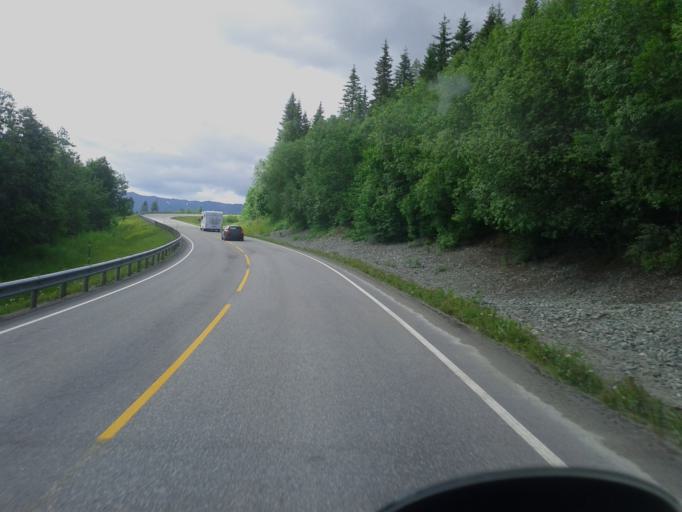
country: NO
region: Nord-Trondelag
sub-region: Grong
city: Grong
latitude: 64.5393
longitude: 12.4462
